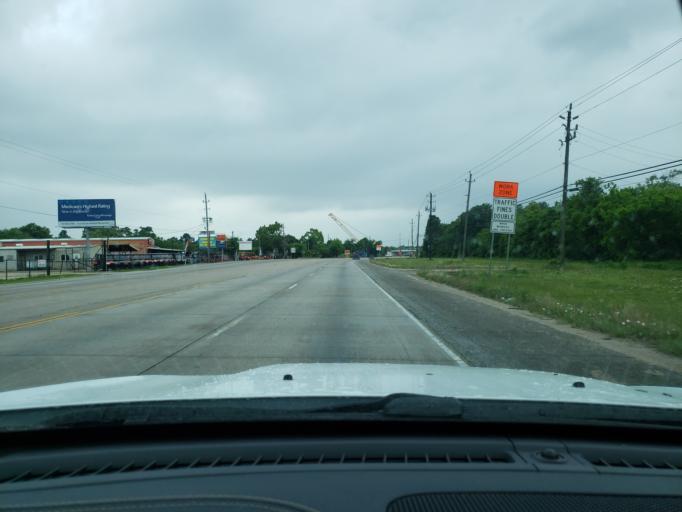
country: US
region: Texas
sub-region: Chambers County
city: Mont Belvieu
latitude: 29.7765
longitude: -94.9136
